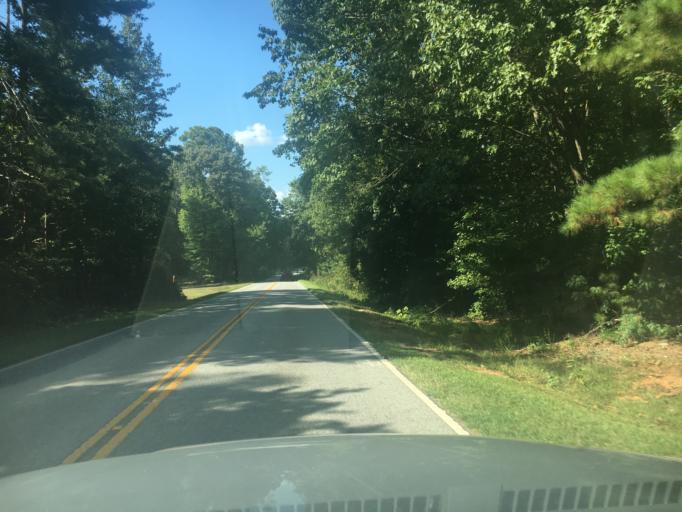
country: US
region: South Carolina
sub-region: Greenwood County
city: Greenwood
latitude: 34.2377
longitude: -82.1801
